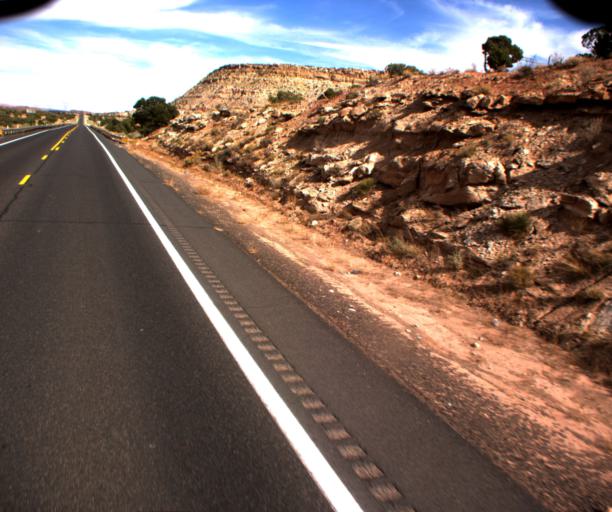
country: US
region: Arizona
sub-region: Navajo County
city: Kayenta
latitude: 36.6840
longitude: -110.3805
